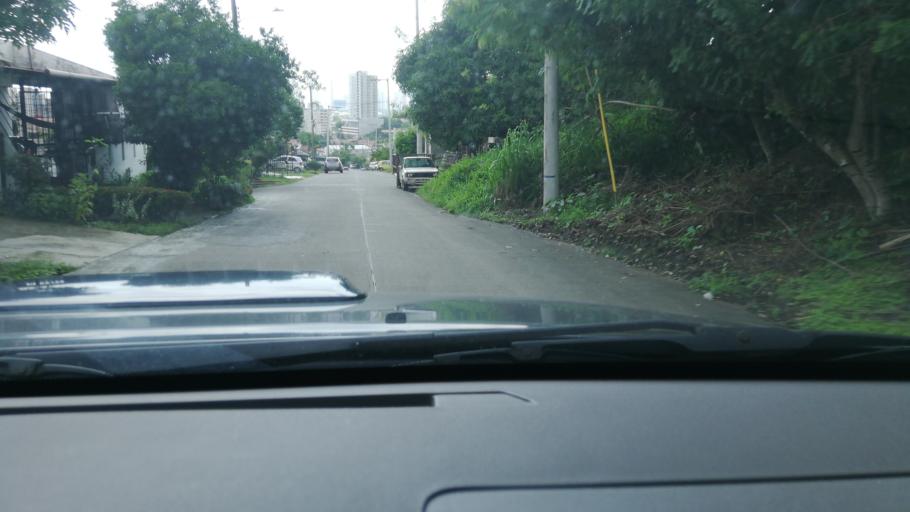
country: PA
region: Panama
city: San Miguelito
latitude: 9.0505
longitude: -79.4776
